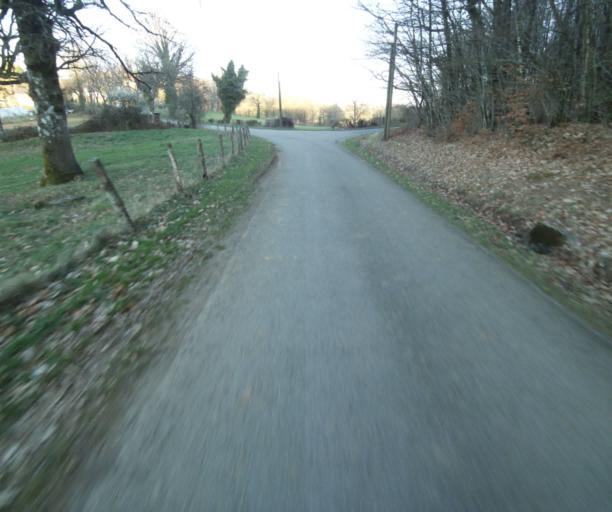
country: FR
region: Limousin
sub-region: Departement de la Correze
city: Seilhac
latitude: 45.3538
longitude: 1.7189
